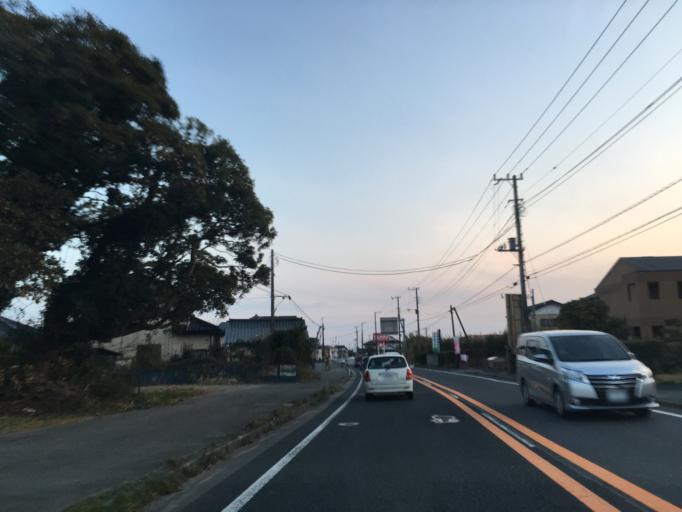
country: JP
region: Ibaraki
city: Kitaibaraki
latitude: 36.8019
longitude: 140.7585
